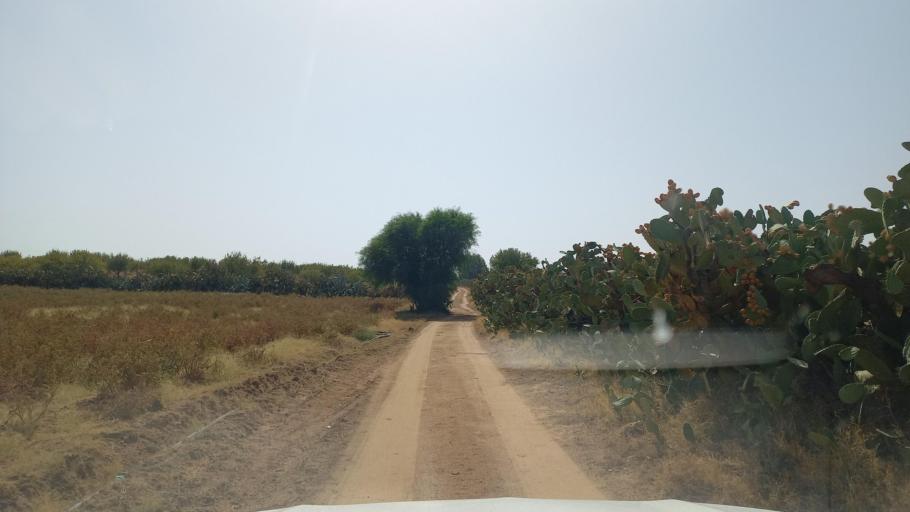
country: TN
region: Al Qasrayn
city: Kasserine
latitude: 35.2349
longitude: 9.0507
